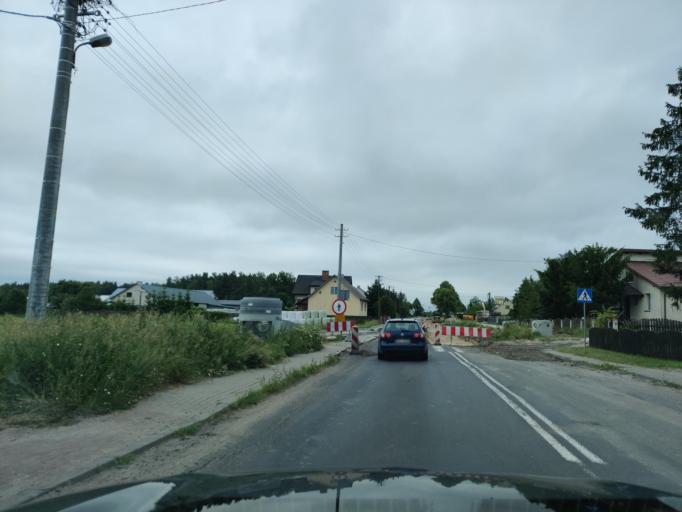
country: PL
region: Warmian-Masurian Voivodeship
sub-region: Powiat szczycienski
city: Rozogi
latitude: 53.4778
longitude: 21.3655
